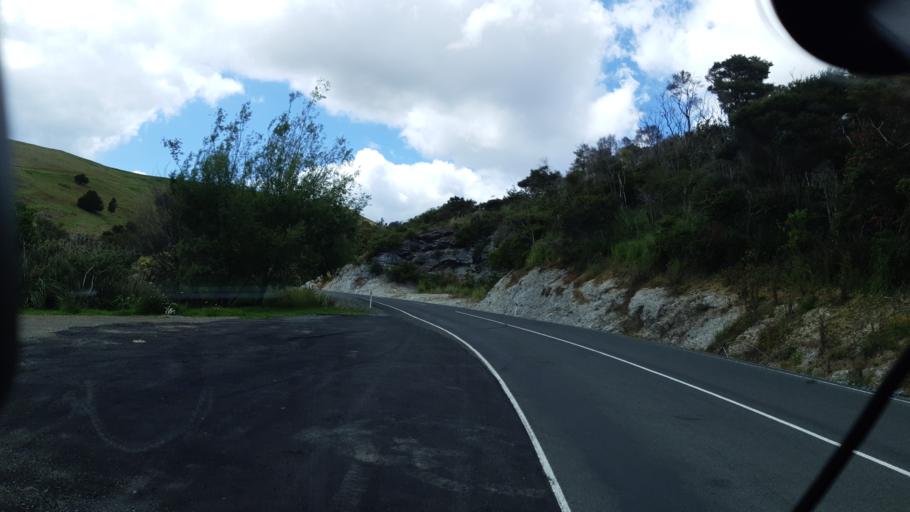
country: NZ
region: Northland
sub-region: Far North District
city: Taipa
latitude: -35.2434
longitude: 173.5342
